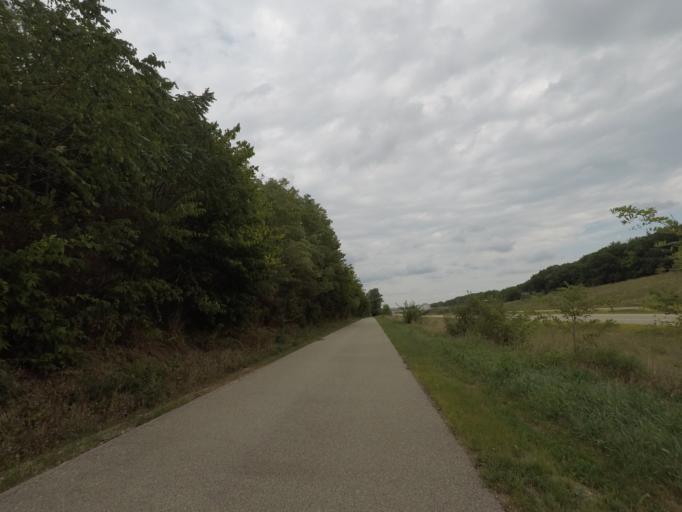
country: US
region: Wisconsin
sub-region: Jefferson County
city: Lake Koshkonong
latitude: 42.8802
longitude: -88.8812
